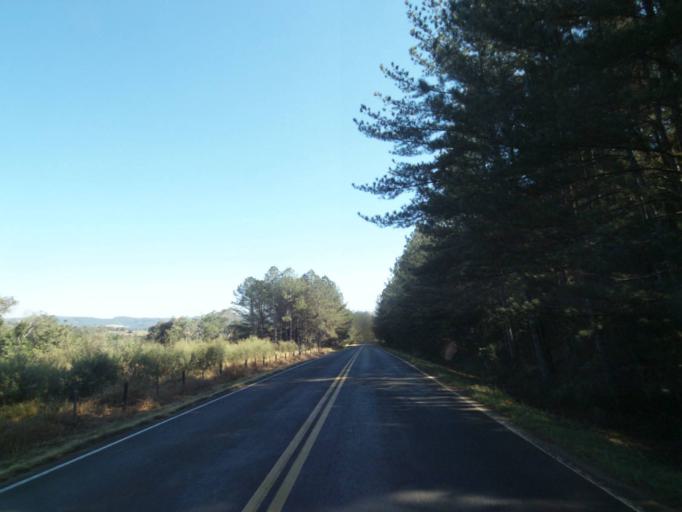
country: BR
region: Parana
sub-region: Tibagi
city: Tibagi
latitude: -24.4788
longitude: -50.4820
